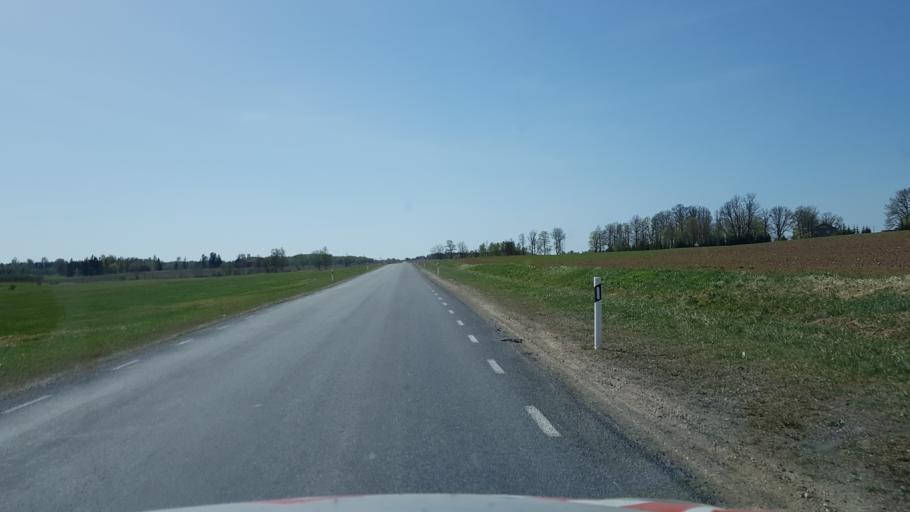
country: EE
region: Tartu
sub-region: Elva linn
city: Elva
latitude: 58.2012
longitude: 26.3765
